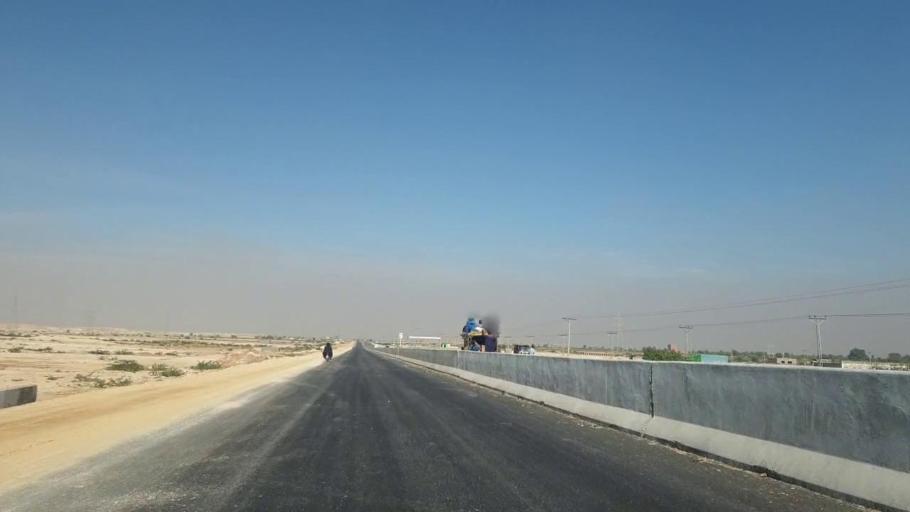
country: PK
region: Sindh
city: Jamshoro
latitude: 25.5095
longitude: 68.2734
